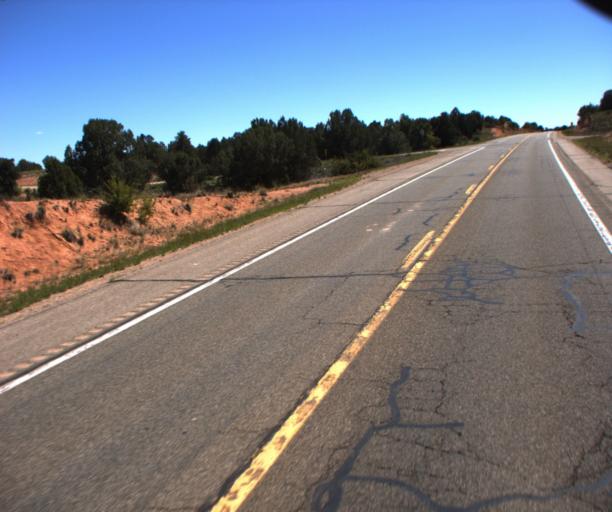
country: US
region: Arizona
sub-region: Yavapai County
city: Paulden
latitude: 34.9747
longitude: -112.4049
